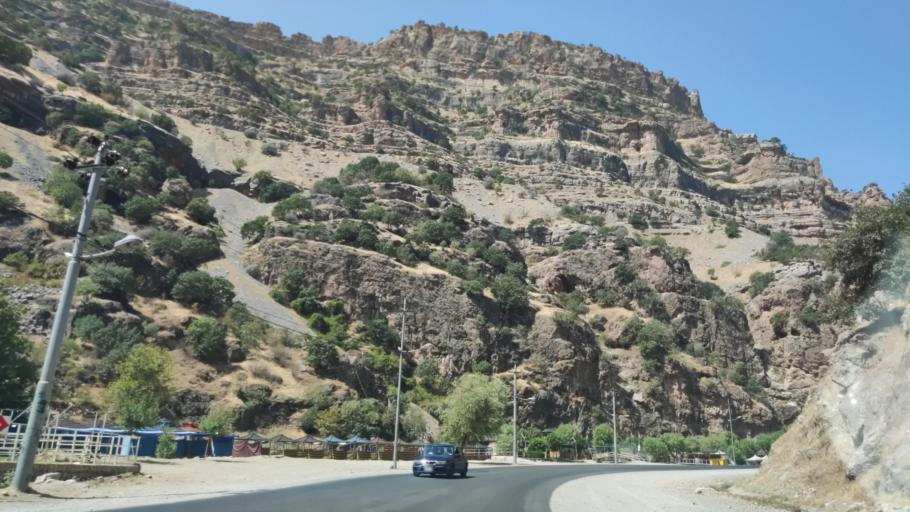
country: IQ
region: Arbil
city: Ruwandiz
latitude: 36.6277
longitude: 44.4517
